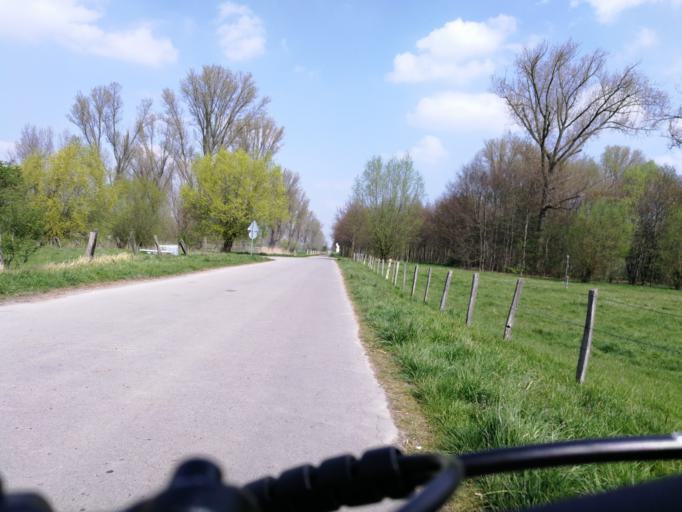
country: DE
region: North Rhine-Westphalia
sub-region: Regierungsbezirk Dusseldorf
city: Dormagen
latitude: 51.1433
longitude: 6.8234
